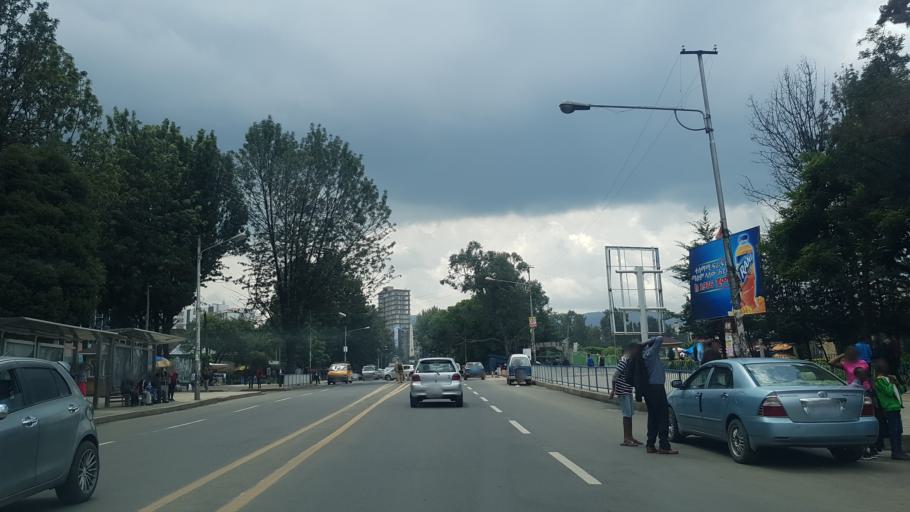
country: ET
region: Adis Abeba
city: Addis Ababa
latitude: 9.0403
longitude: 38.7621
